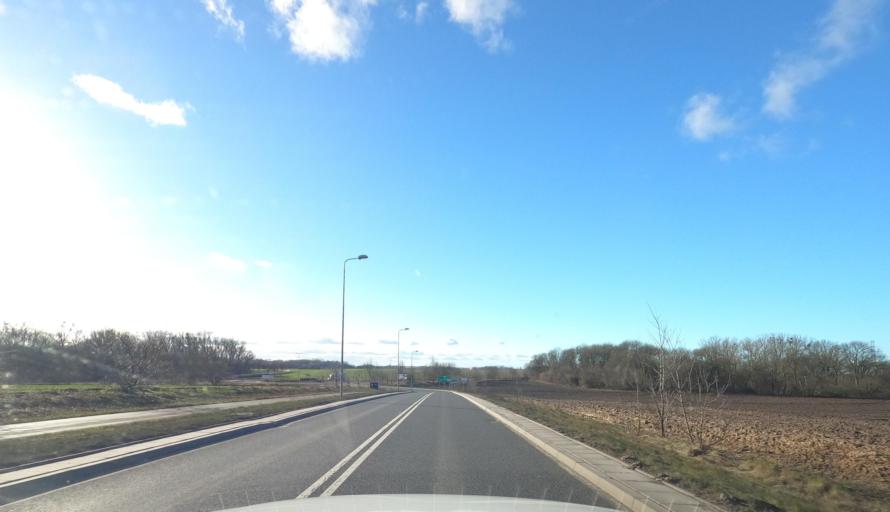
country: PL
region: West Pomeranian Voivodeship
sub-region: Powiat pyrzycki
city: Warnice
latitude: 53.3018
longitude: 14.9990
